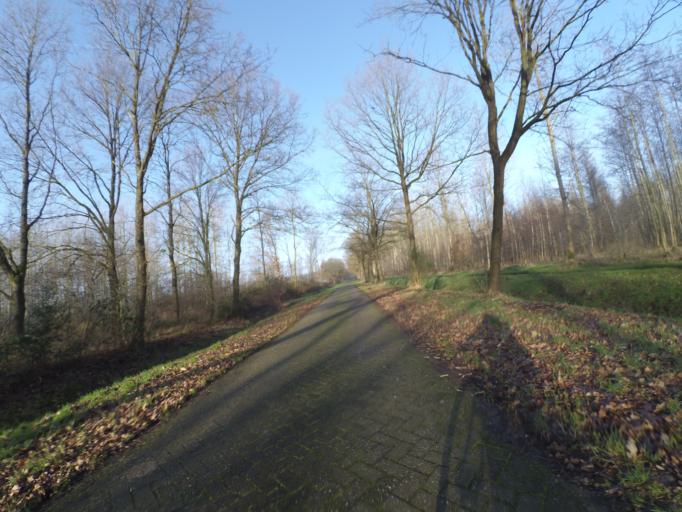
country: NL
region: Drenthe
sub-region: Gemeente Borger-Odoorn
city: Borger
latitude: 52.8432
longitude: 6.7061
